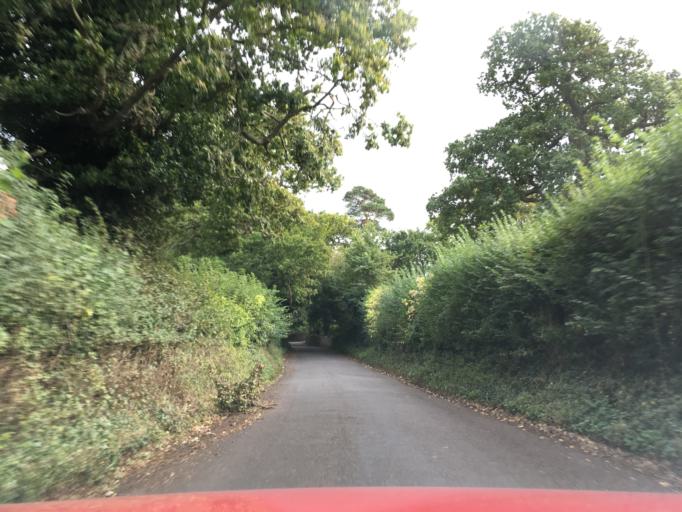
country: GB
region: England
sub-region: South Gloucestershire
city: Alveston
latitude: 51.5742
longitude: -2.5500
